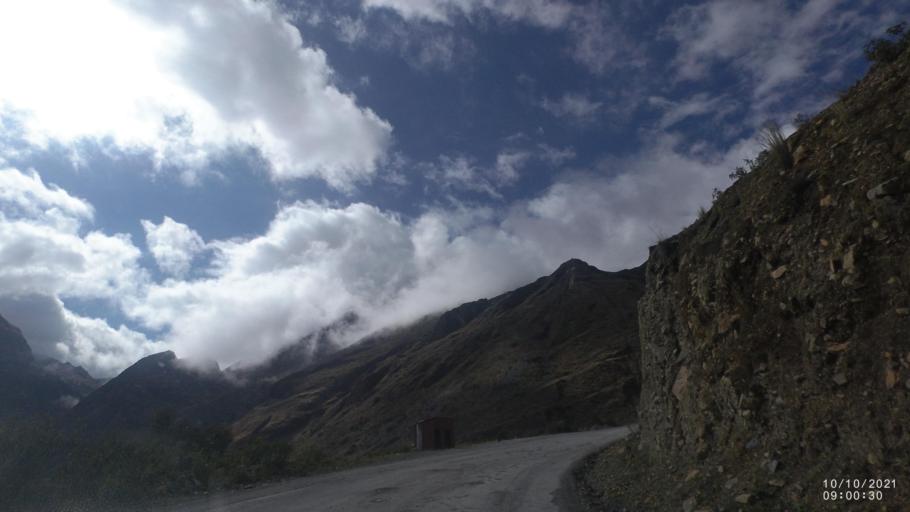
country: BO
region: La Paz
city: Quime
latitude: -16.9974
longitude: -67.2612
